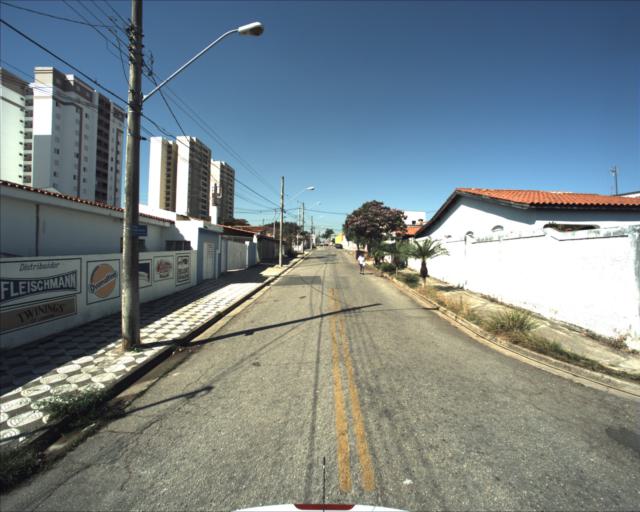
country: BR
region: Sao Paulo
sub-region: Sorocaba
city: Sorocaba
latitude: -23.4922
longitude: -47.4379
